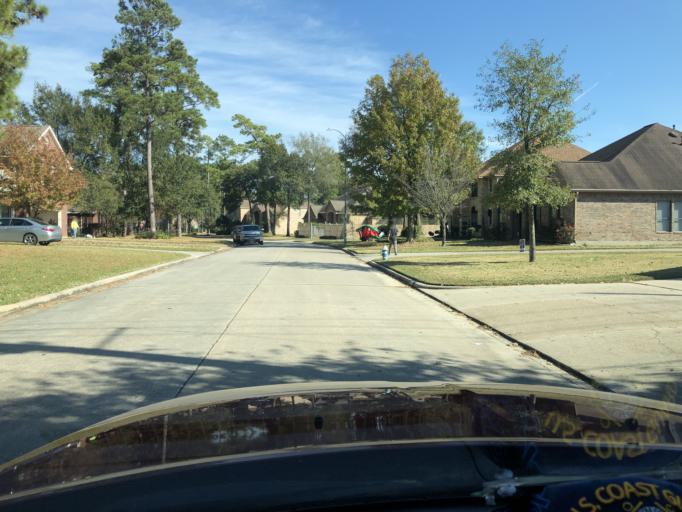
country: US
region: Texas
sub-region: Harris County
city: Tomball
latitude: 30.0186
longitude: -95.5549
